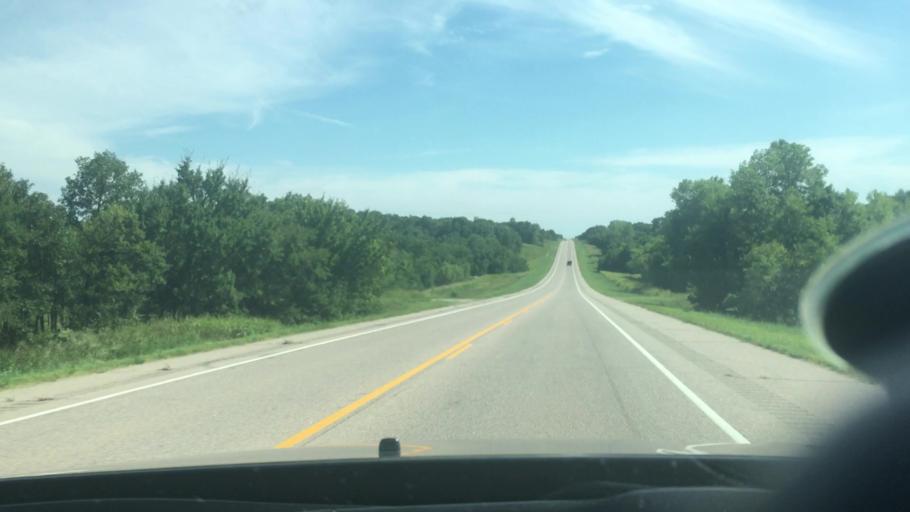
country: US
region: Oklahoma
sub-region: Seminole County
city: Maud
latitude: 35.1131
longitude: -96.6789
